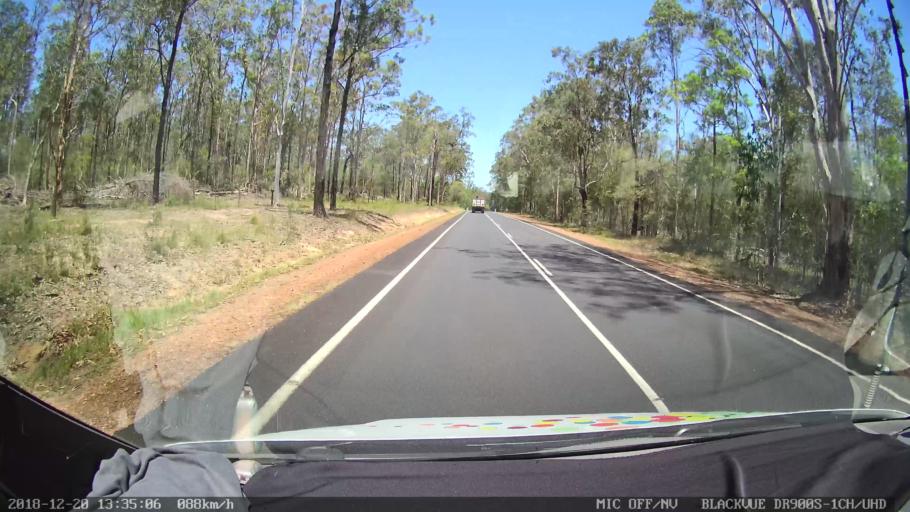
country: AU
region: New South Wales
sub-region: Clarence Valley
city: Gordon
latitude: -29.2661
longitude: 152.9882
